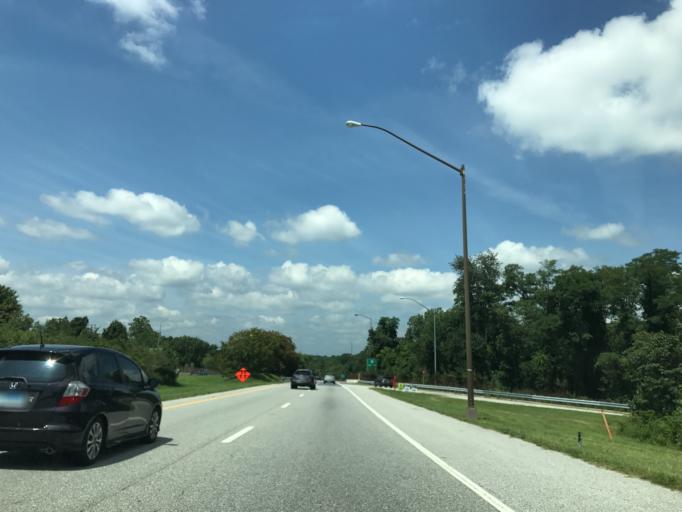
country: US
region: Maryland
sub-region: Howard County
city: Columbia
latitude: 39.2248
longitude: -76.8436
